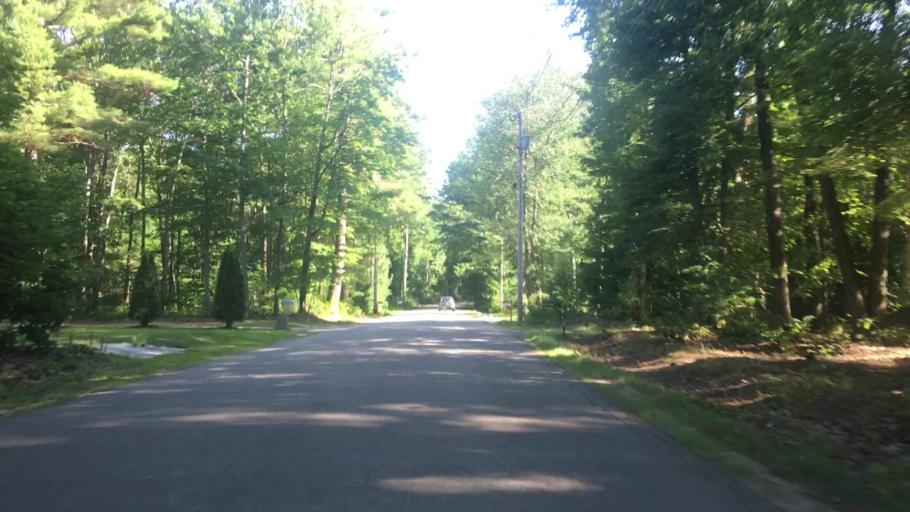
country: US
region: Maine
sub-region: Cumberland County
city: Gorham
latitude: 43.7211
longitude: -70.5153
